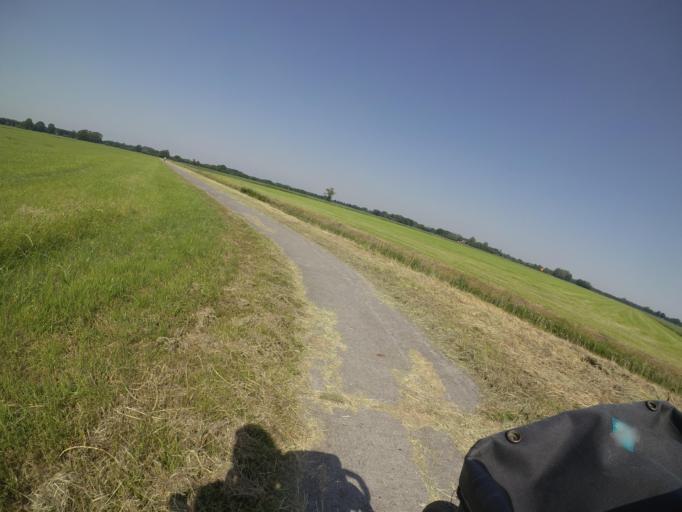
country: NL
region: Drenthe
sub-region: Gemeente De Wolden
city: Ruinen
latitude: 52.6810
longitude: 6.3224
